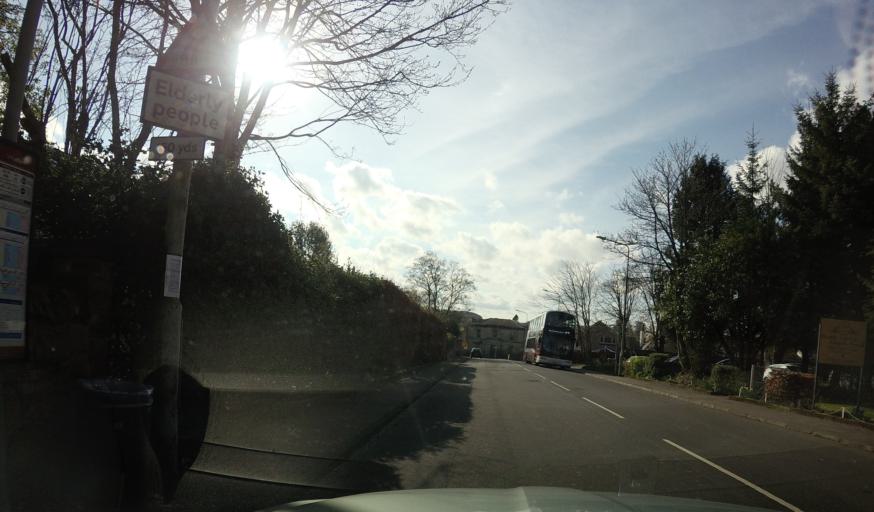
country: GB
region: Scotland
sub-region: Midlothian
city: Penicuik
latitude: 55.8263
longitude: -3.2249
